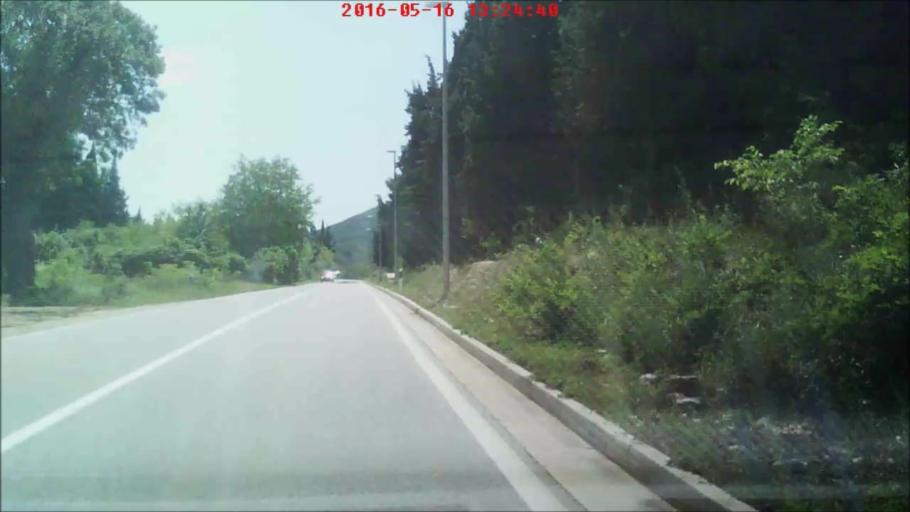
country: HR
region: Dubrovacko-Neretvanska
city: Ston
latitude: 42.8425
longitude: 17.7016
